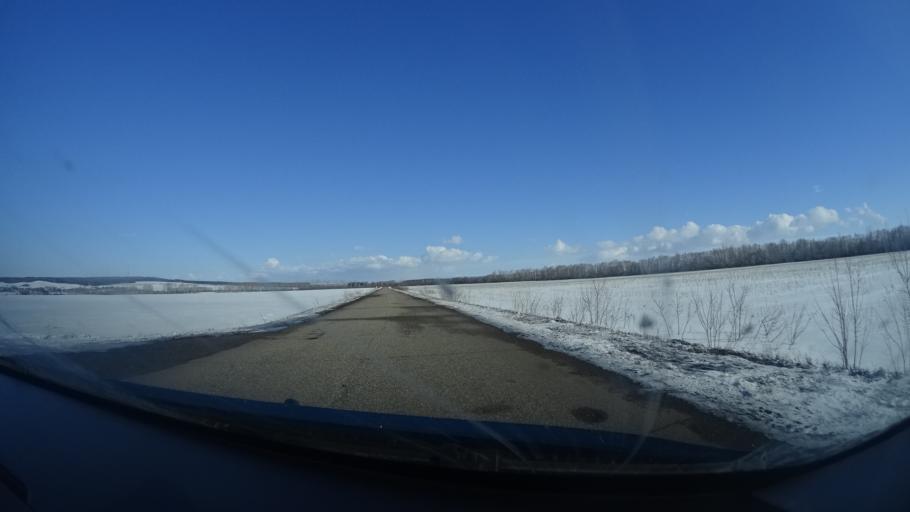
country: RU
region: Bashkortostan
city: Chishmy
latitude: 54.5910
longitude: 55.3139
